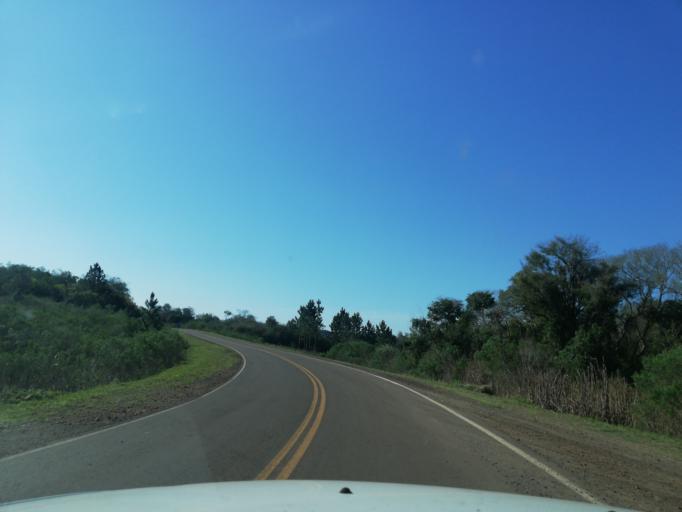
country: AR
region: Misiones
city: Arroyo del Medio
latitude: -27.6869
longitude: -55.3967
